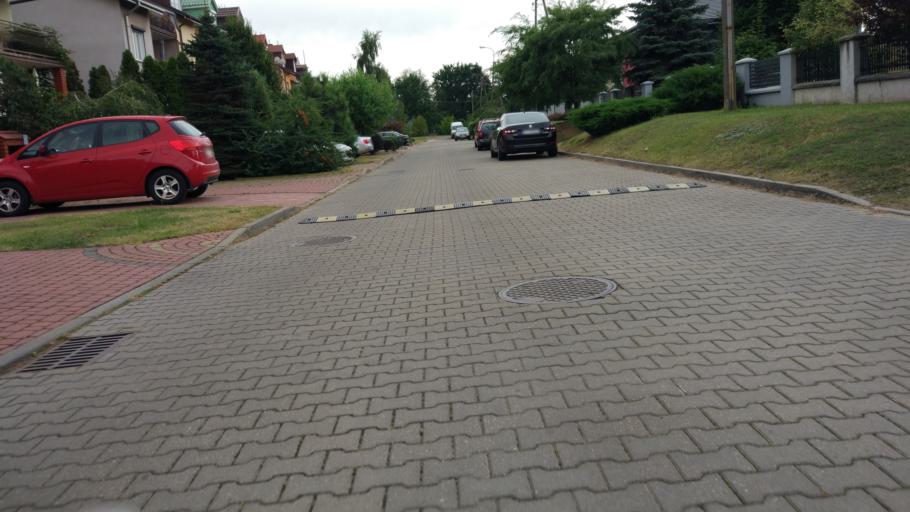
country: PL
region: Masovian Voivodeship
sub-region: Plock
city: Plock
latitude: 52.5281
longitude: 19.7521
